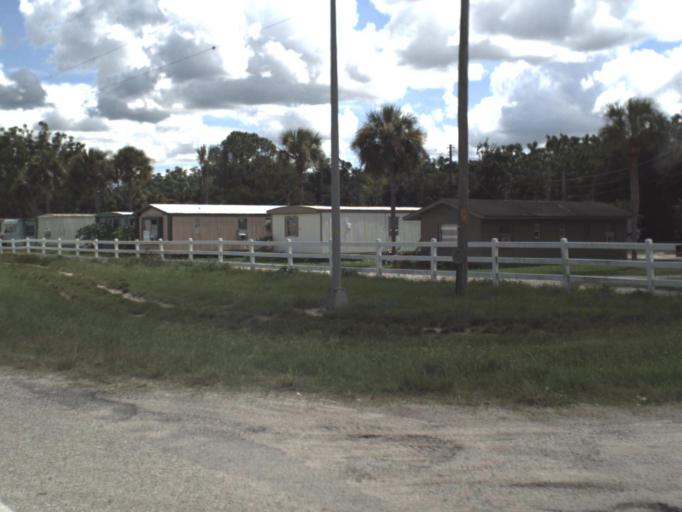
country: US
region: Florida
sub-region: Polk County
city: Willow Oak
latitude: 27.9180
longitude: -82.0244
